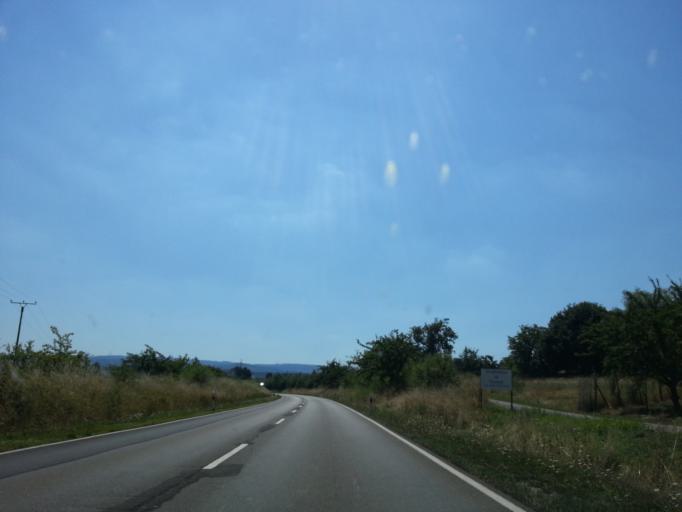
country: DE
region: Rheinland-Pfalz
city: Osann-Monzel
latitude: 49.9205
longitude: 6.9442
